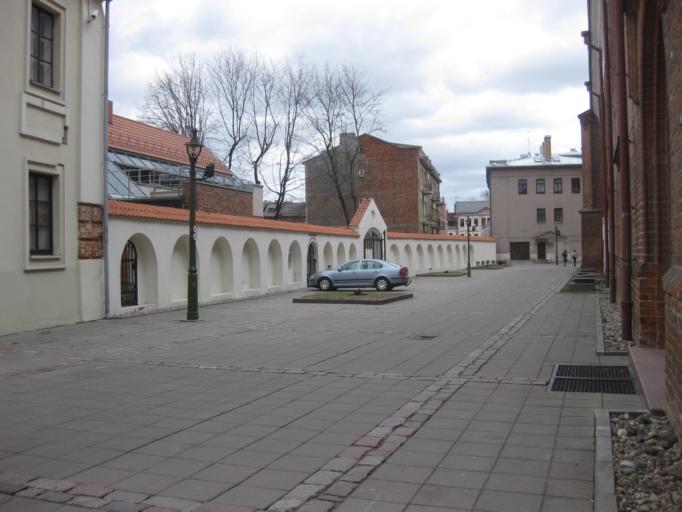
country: LT
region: Kauno apskritis
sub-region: Kaunas
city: Kaunas
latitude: 54.8975
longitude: 23.8886
